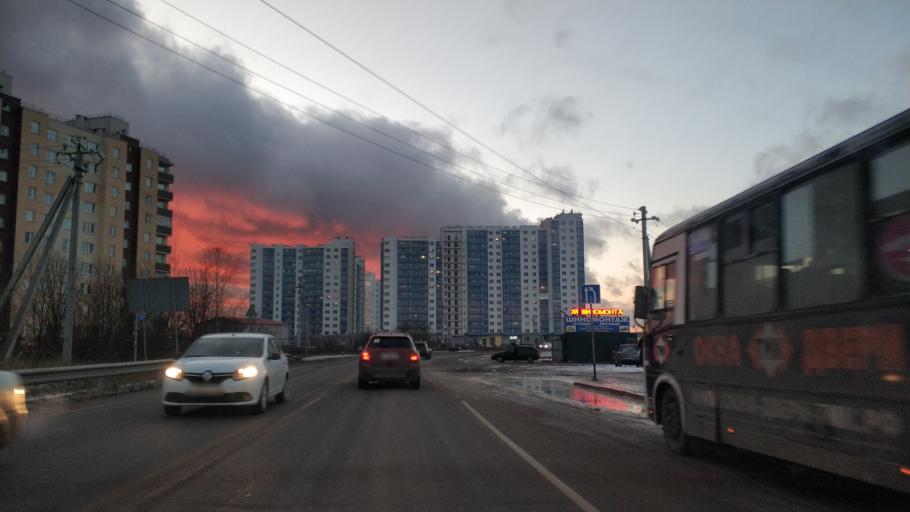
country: RU
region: St.-Petersburg
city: Pontonnyy
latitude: 59.8009
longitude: 30.6375
